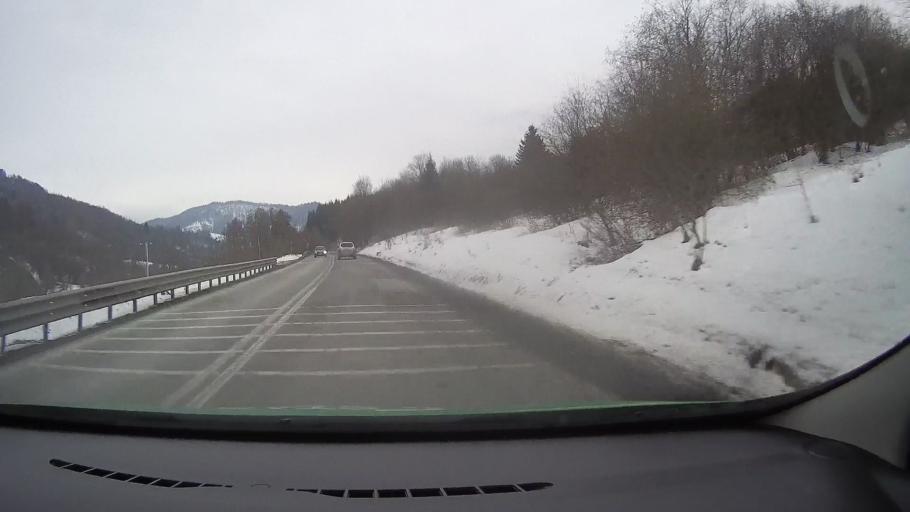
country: RO
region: Brasov
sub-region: Oras Predeal
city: Predeal
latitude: 45.5272
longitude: 25.5002
